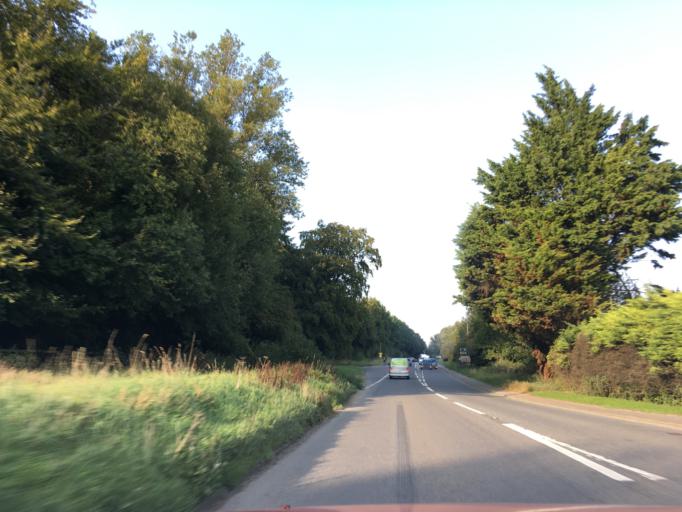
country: GB
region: England
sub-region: Gloucestershire
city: Bourton on the Water
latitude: 51.8872
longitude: -1.7682
